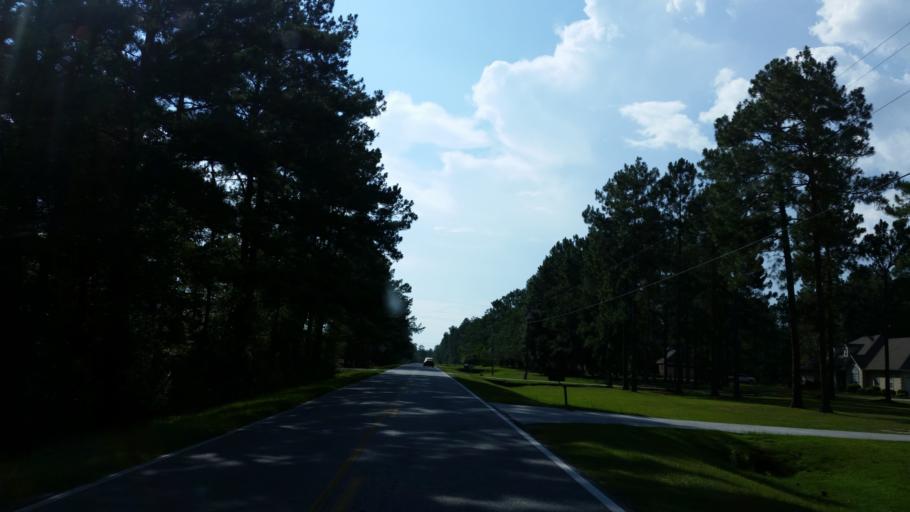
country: US
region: Georgia
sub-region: Lowndes County
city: Remerton
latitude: 30.8986
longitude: -83.3735
